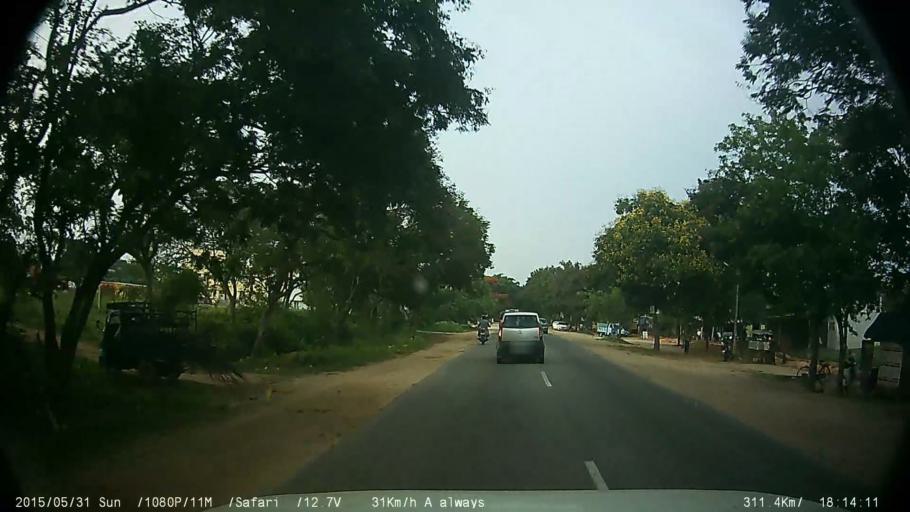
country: IN
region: Karnataka
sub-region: Mysore
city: Nanjangud
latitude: 12.1056
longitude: 76.6723
